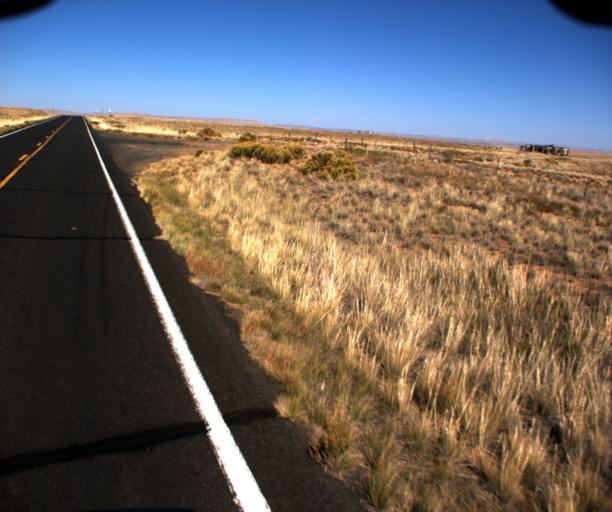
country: US
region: Arizona
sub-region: Navajo County
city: First Mesa
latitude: 35.6384
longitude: -110.4848
